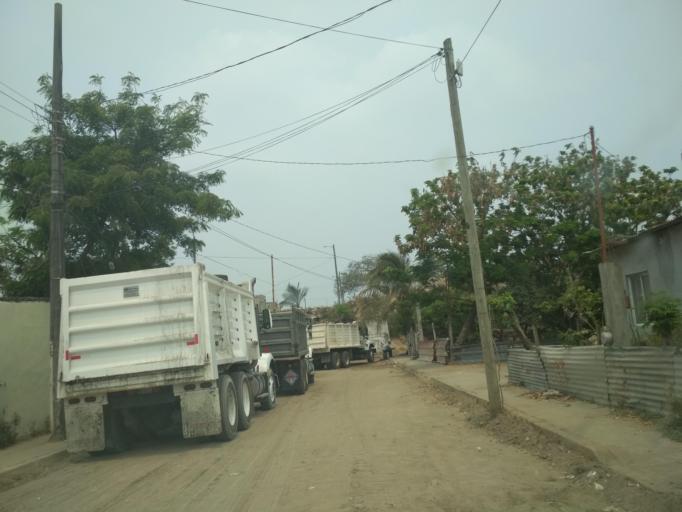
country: MX
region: Veracruz
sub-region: Veracruz
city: Rio Medio [Granja]
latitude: 19.2065
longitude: -96.2104
